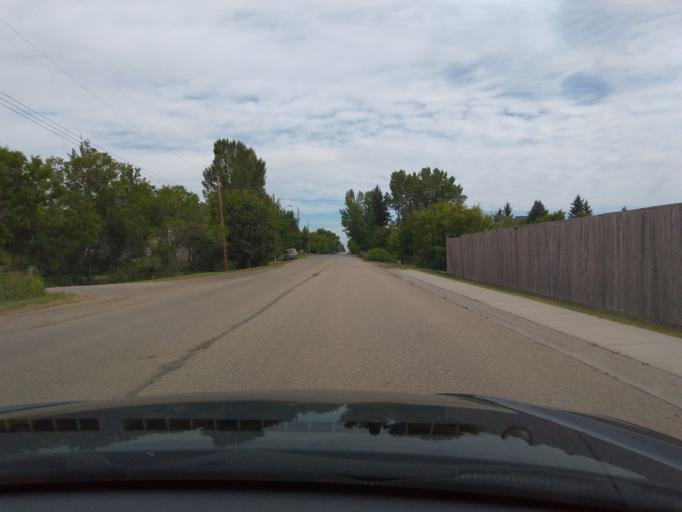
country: CA
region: Alberta
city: Didsbury
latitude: 51.6526
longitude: -114.1433
